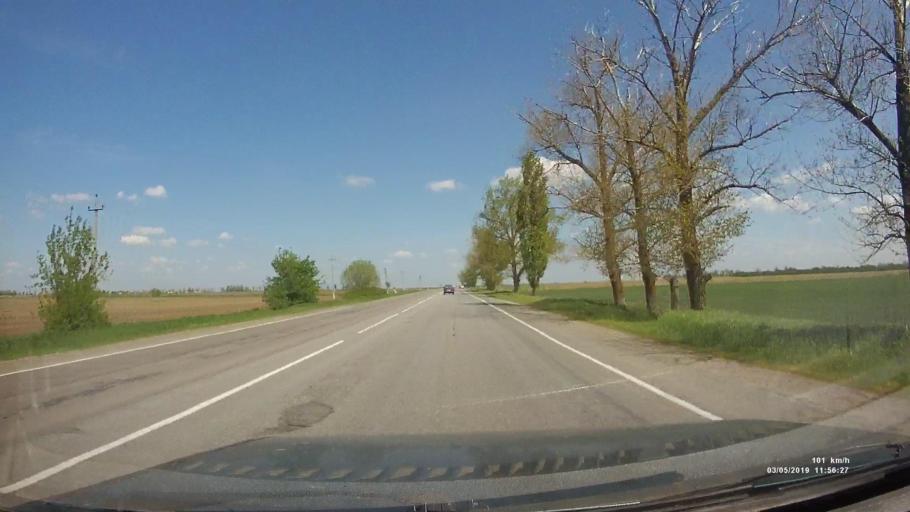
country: RU
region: Rostov
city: Bagayevskaya
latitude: 47.1947
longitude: 40.3011
